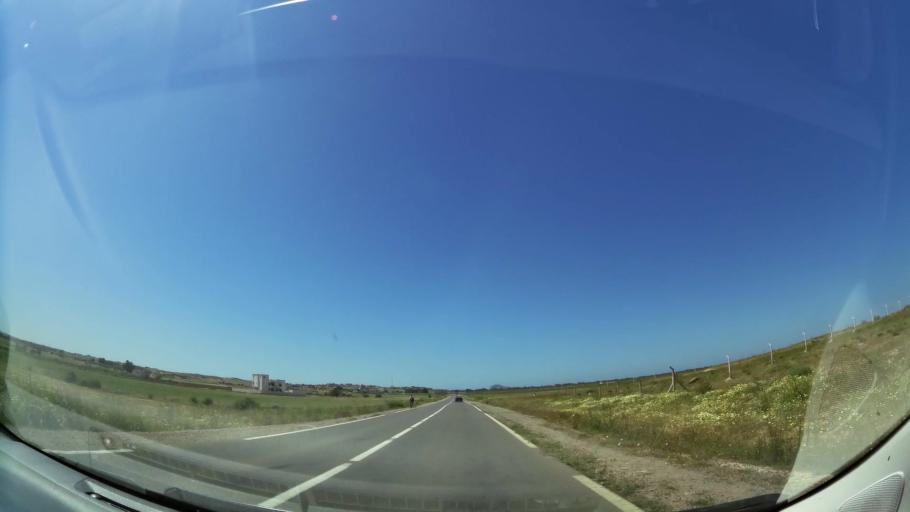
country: MA
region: Oriental
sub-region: Berkane-Taourirt
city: Madagh
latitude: 35.1139
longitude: -2.3659
